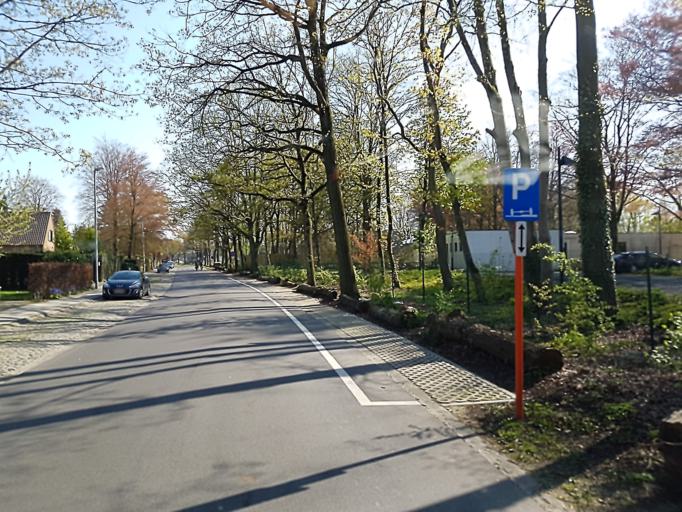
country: BE
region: Flanders
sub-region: Provincie Oost-Vlaanderen
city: Sint-Niklaas
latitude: 51.1757
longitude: 4.1818
